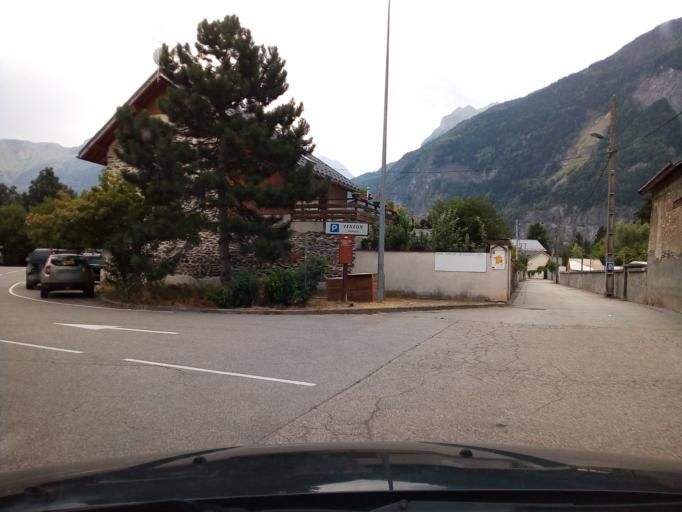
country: FR
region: Rhone-Alpes
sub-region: Departement de l'Isere
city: Huez
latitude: 45.0544
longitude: 6.0320
